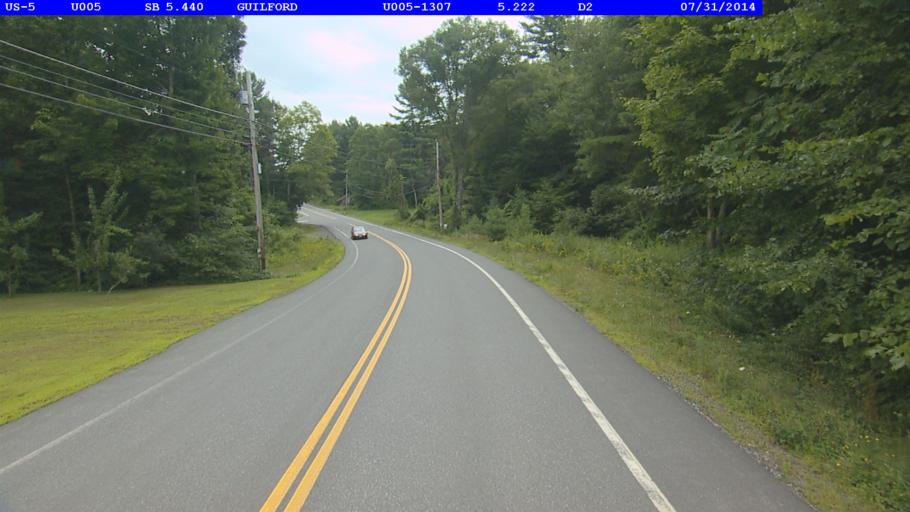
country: US
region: Vermont
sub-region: Windham County
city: Brattleboro
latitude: 42.8055
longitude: -72.5666
